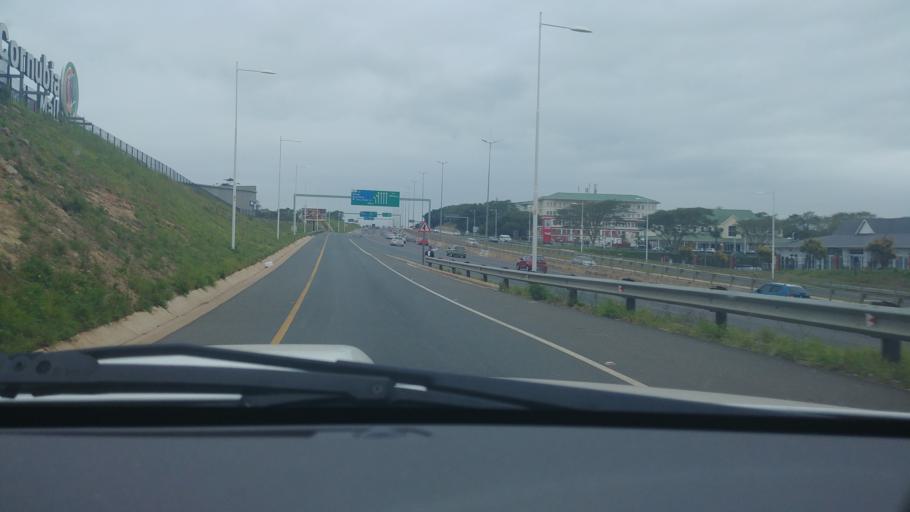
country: ZA
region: KwaZulu-Natal
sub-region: eThekwini Metropolitan Municipality
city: Durban
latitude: -29.7120
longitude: 31.0524
